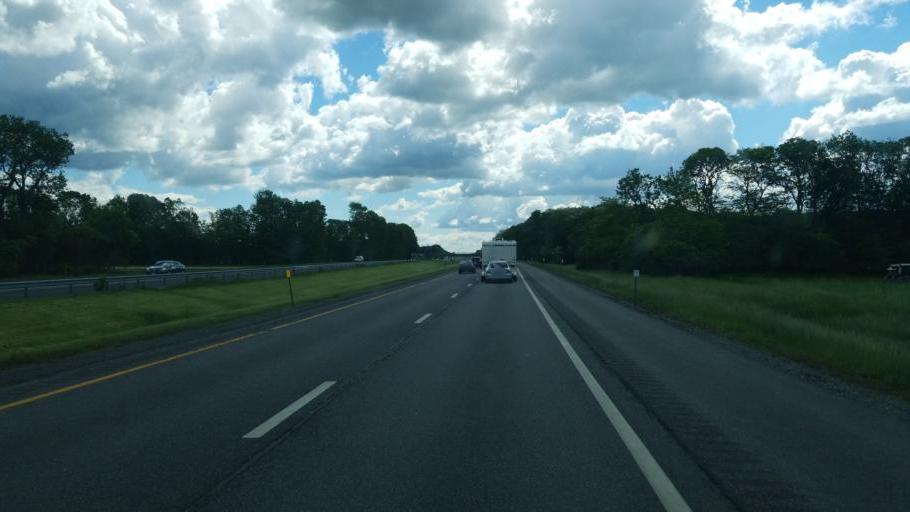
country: US
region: New York
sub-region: Onondaga County
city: Minoa
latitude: 43.0923
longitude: -75.9607
